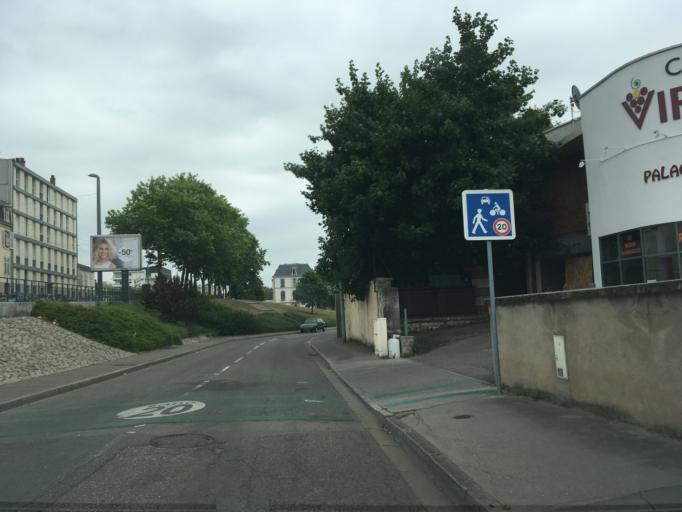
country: FR
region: Lorraine
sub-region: Departement de Meurthe-et-Moselle
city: Saint-Max
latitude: 48.6985
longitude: 6.2012
